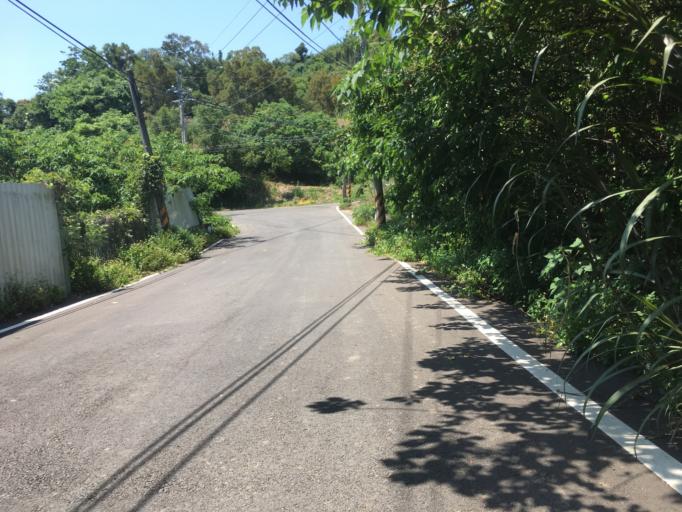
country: TW
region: Taiwan
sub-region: Hsinchu
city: Hsinchu
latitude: 24.7362
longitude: 120.9793
